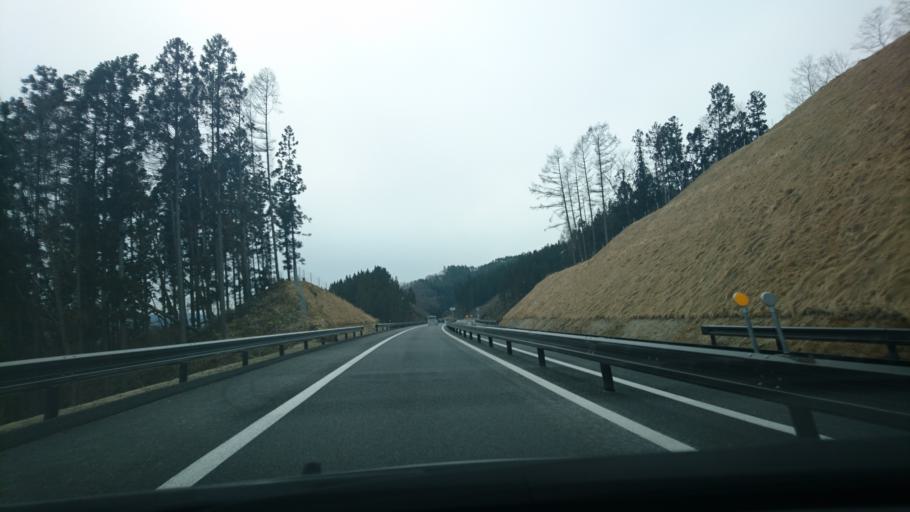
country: JP
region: Iwate
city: Tono
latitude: 39.3024
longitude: 141.5342
